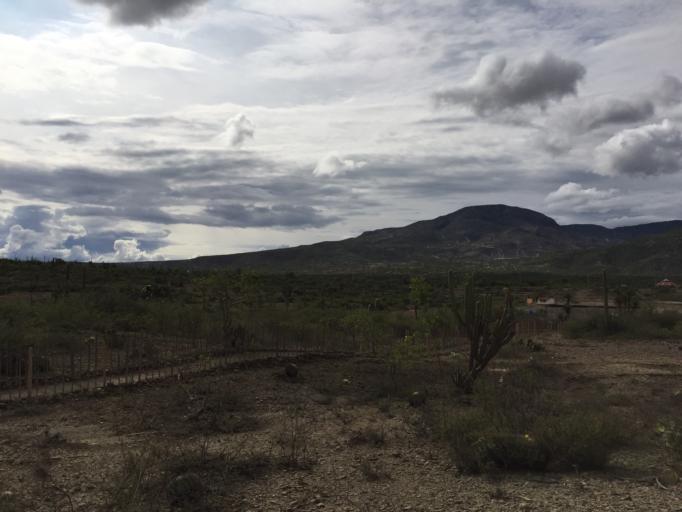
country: MX
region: Oaxaca
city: Santiago Chazumba
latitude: 18.3078
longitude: -97.6165
